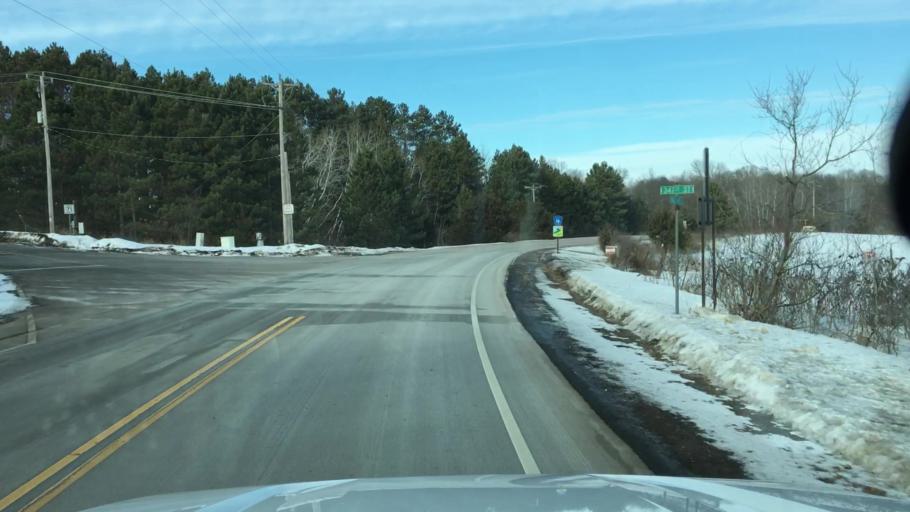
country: US
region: Wisconsin
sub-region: Polk County
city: Saint Croix Falls
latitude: 45.4517
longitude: -92.6716
